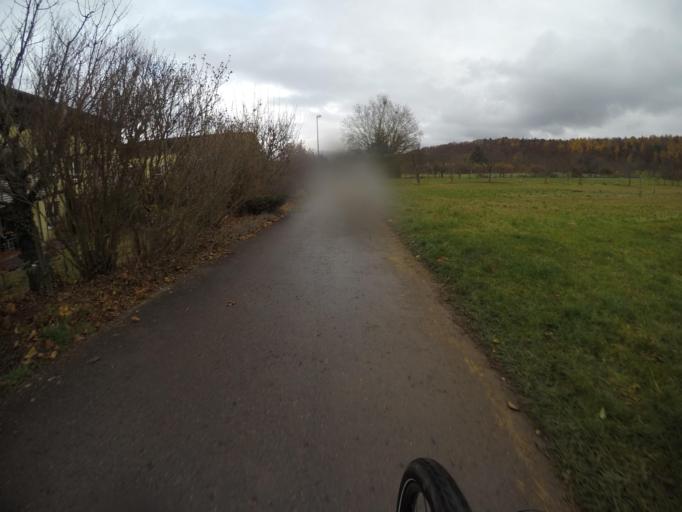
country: DE
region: Baden-Wuerttemberg
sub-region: Regierungsbezirk Stuttgart
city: Gerlingen
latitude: 48.7984
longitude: 9.0766
